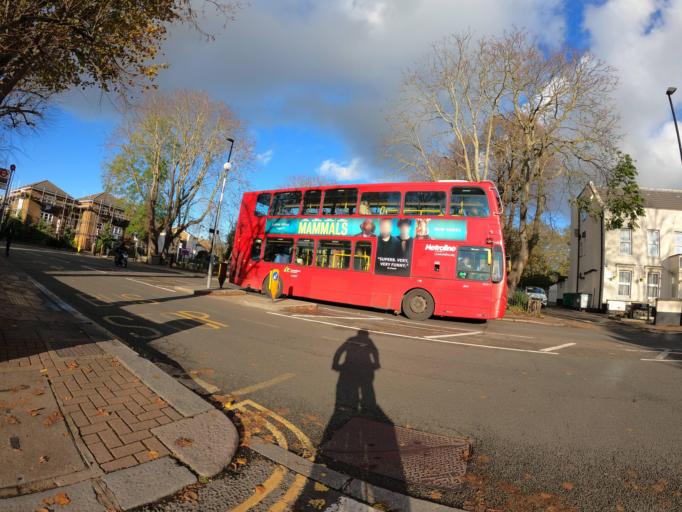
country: GB
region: England
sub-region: Greater London
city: Brentford
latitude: 51.4863
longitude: -0.3080
